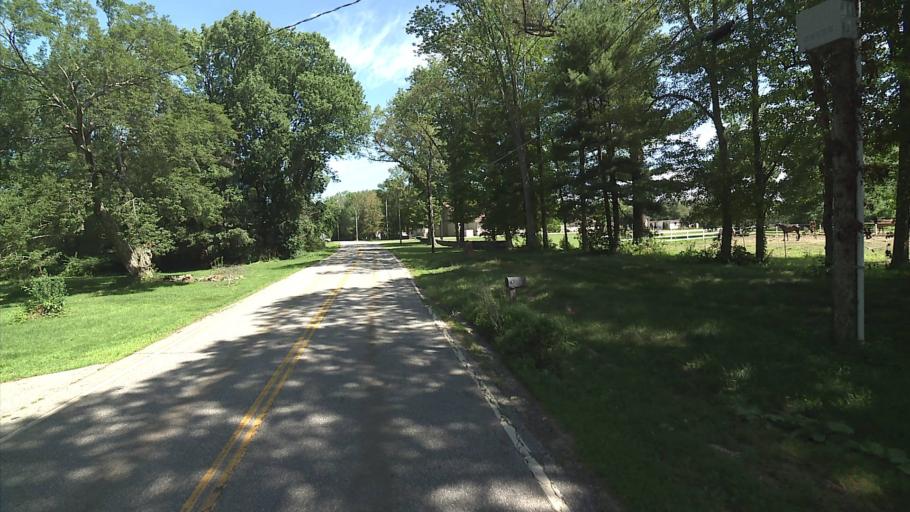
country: US
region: Connecticut
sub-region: Windham County
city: Windham
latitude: 41.7066
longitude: -72.0675
